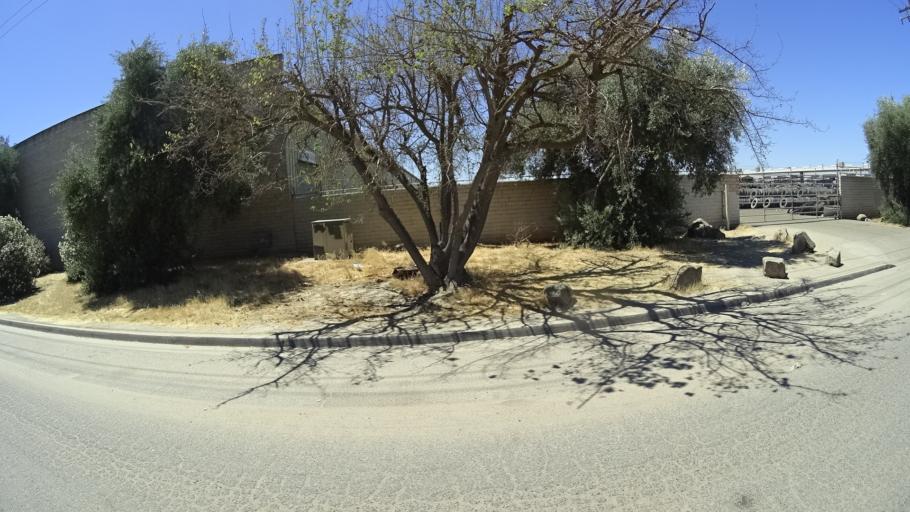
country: US
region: California
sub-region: Fresno County
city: Fresno
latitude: 36.6996
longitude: -119.7824
